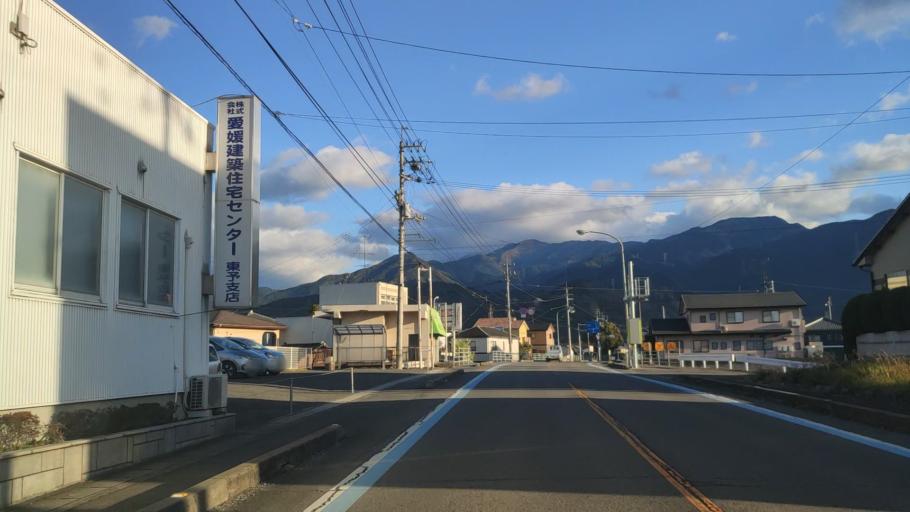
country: JP
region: Ehime
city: Saijo
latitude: 33.9085
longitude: 133.1835
